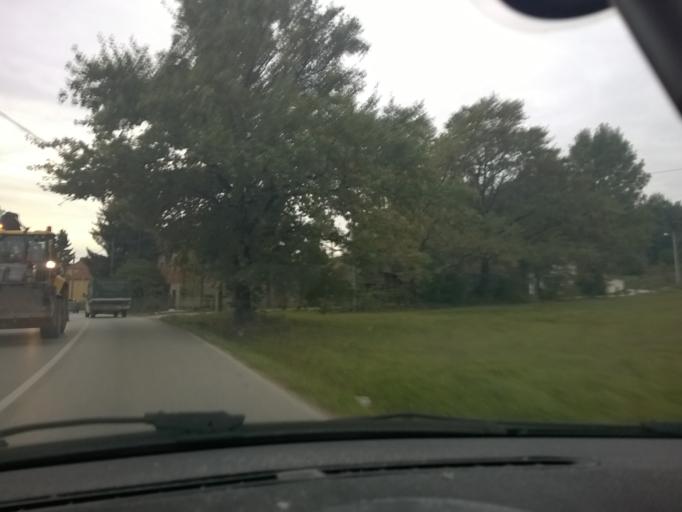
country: HR
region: Zagrebacka
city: Pojatno
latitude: 45.9106
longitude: 15.8078
